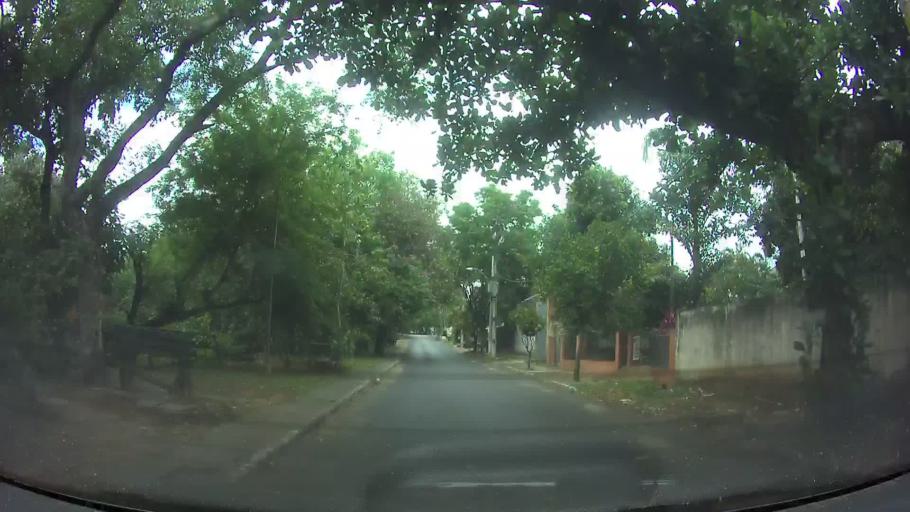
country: PY
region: Asuncion
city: Asuncion
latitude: -25.3014
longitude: -57.5959
